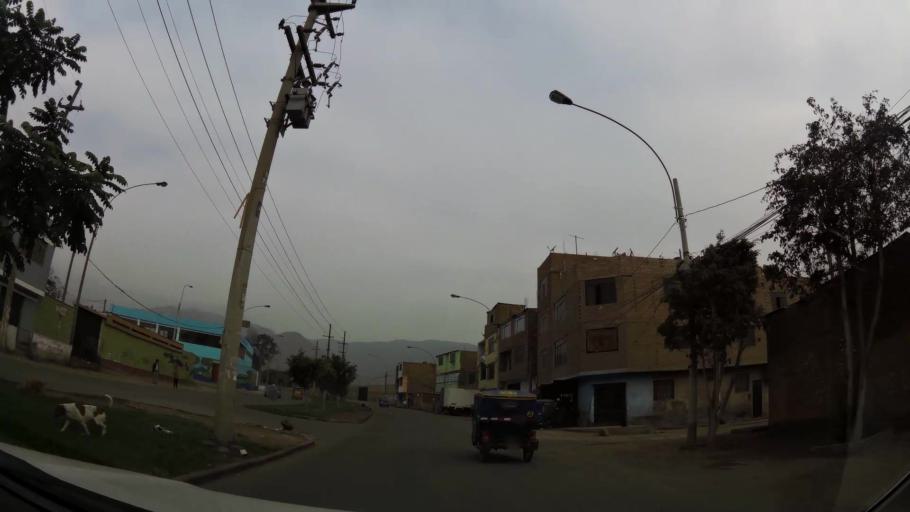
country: PE
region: Lima
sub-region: Lima
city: Independencia
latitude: -11.9776
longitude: -76.9935
